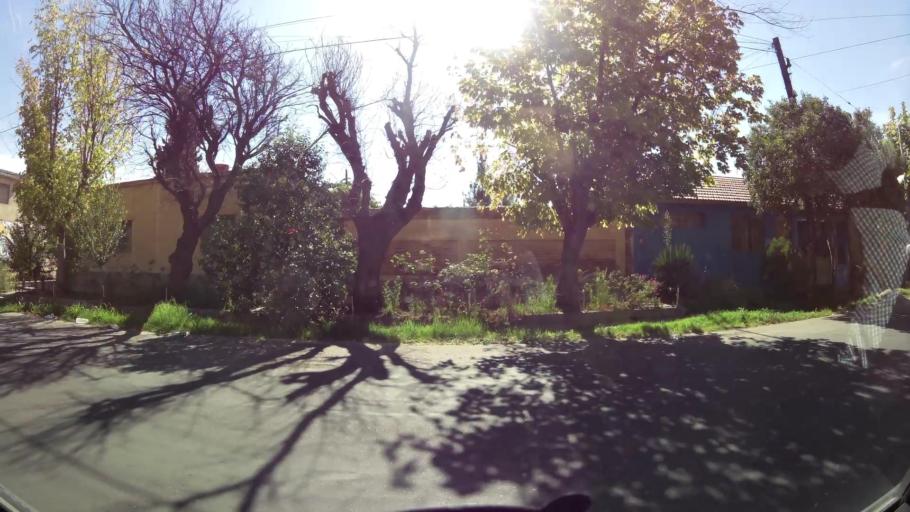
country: AR
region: Mendoza
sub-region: Departamento de Godoy Cruz
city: Godoy Cruz
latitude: -32.9426
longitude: -68.8098
